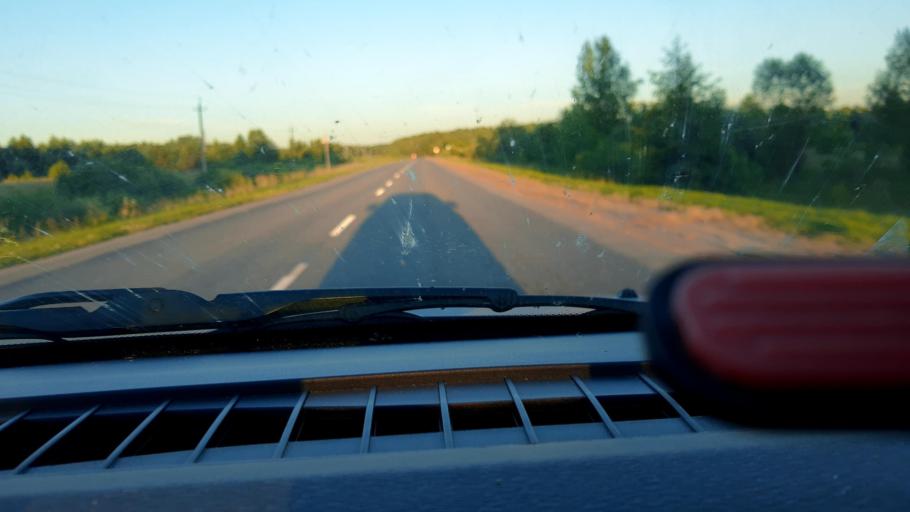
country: RU
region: Nizjnij Novgorod
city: Prudy
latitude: 57.3729
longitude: 46.1633
